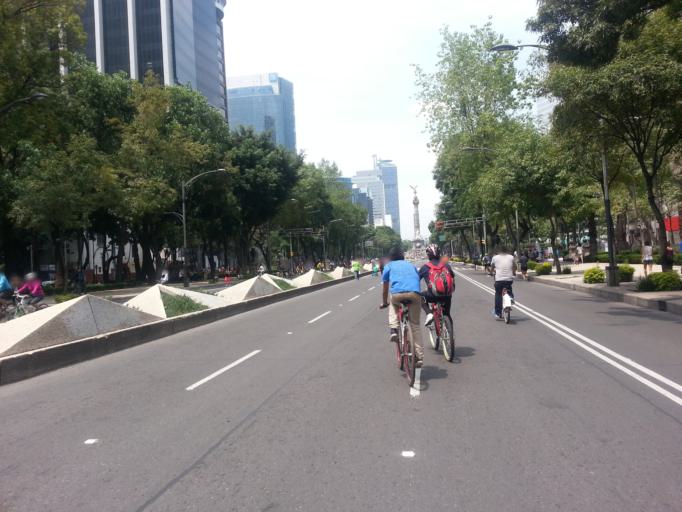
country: MX
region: Mexico City
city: Cuauhtemoc
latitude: 19.4286
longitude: -99.1644
